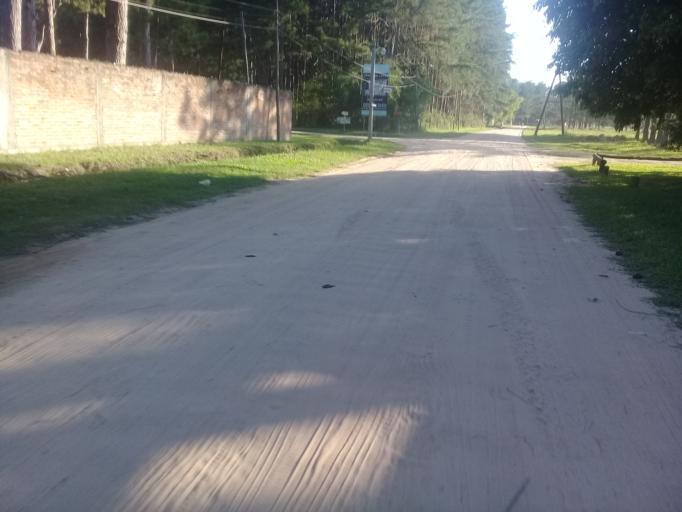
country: AR
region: Corrientes
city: San Luis del Palmar
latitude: -27.4638
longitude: -58.6663
